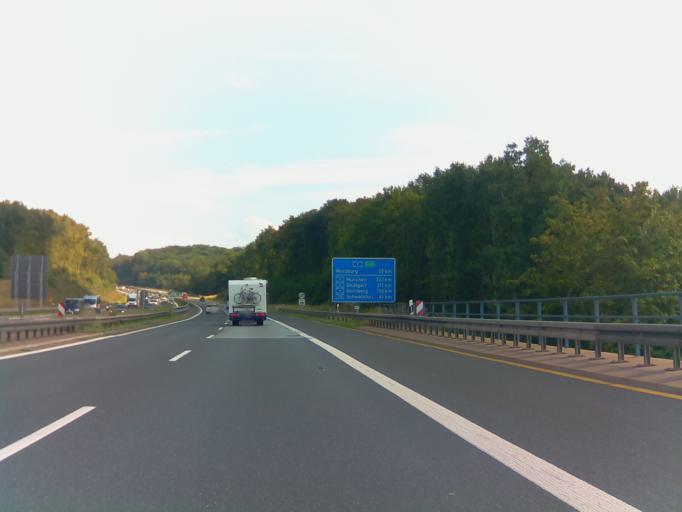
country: DE
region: Bavaria
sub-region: Regierungsbezirk Unterfranken
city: Oberthulba
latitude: 50.1904
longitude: 9.9435
